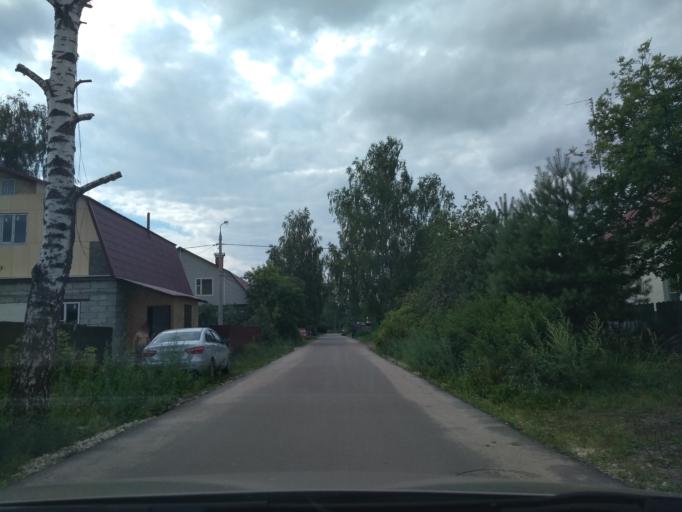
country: RU
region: Moskovskaya
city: Kabanovo
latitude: 55.7858
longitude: 38.9232
